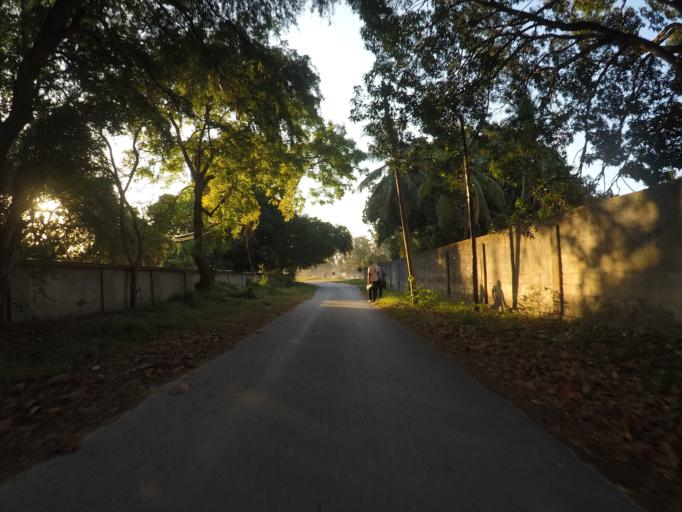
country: TZ
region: Zanzibar Urban/West
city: Zanzibar
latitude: -6.1748
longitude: 39.1974
